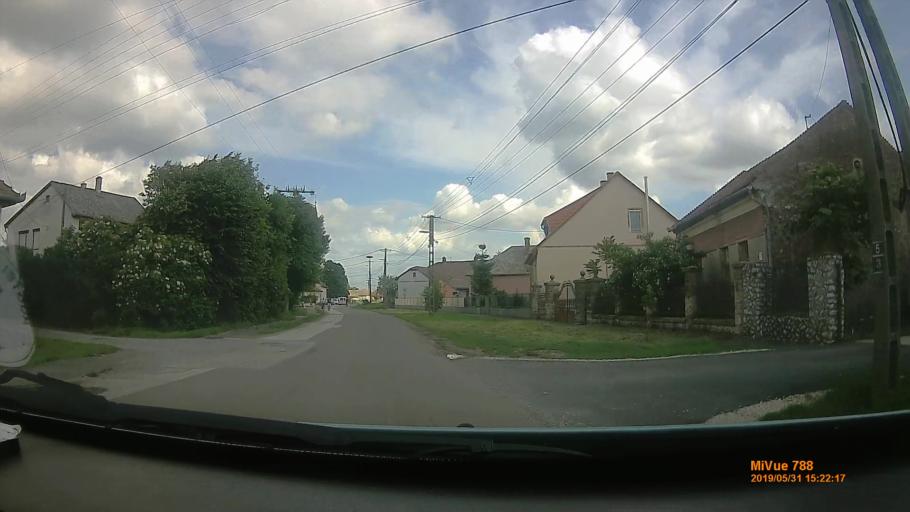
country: HU
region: Borsod-Abauj-Zemplen
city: Taktaharkany
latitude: 48.0831
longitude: 21.1371
